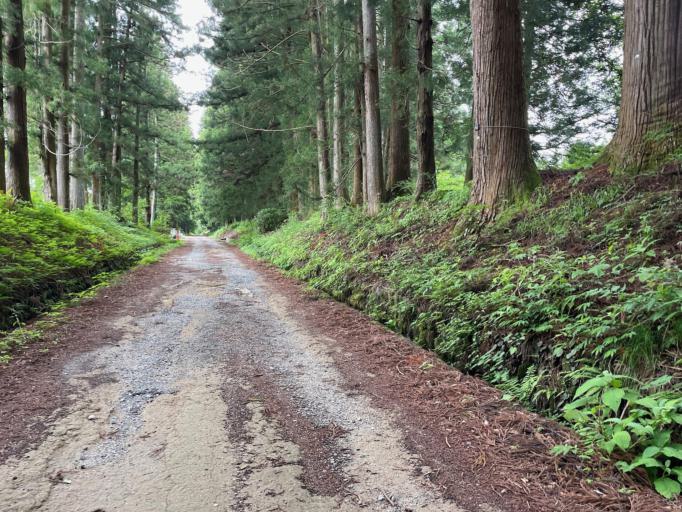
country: JP
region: Tochigi
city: Imaichi
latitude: 36.7336
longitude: 139.6582
